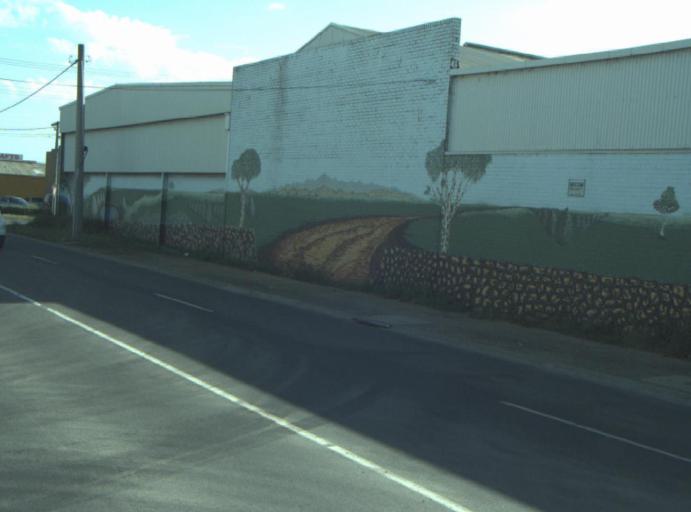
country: AU
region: Victoria
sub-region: Greater Geelong
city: Bell Park
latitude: -38.1150
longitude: 144.3489
